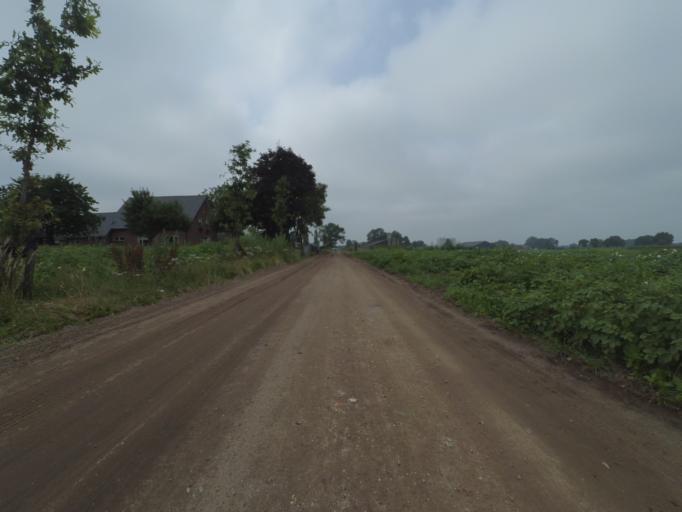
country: NL
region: Gelderland
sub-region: Gemeente Barneveld
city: Kootwijkerbroek
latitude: 52.1257
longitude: 5.6771
